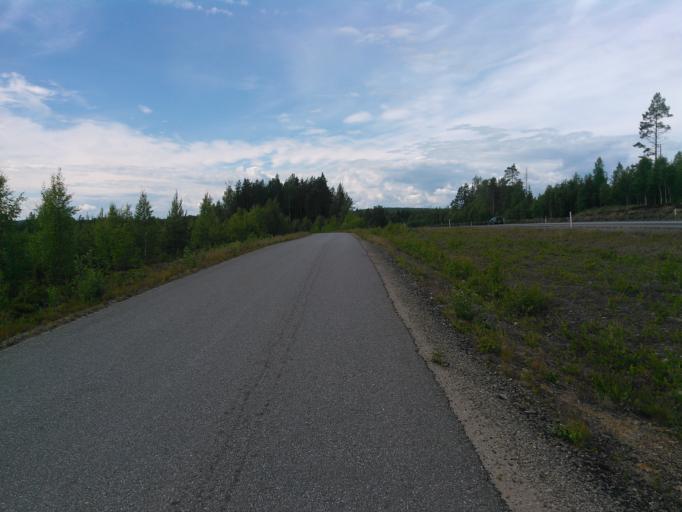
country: SE
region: Vaesterbotten
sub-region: Vannas Kommun
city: Vannasby
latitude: 63.8919
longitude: 19.9882
